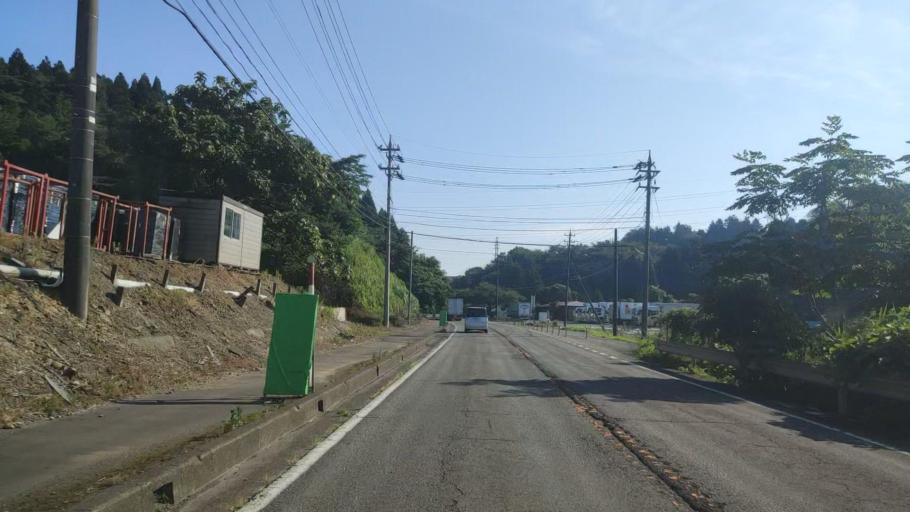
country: JP
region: Fukui
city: Maruoka
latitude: 36.2216
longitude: 136.2772
